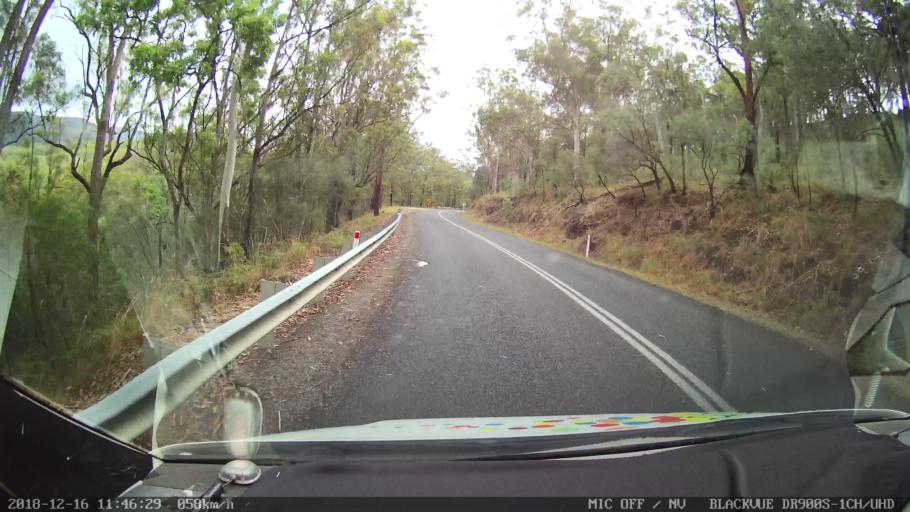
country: AU
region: New South Wales
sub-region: Tenterfield Municipality
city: Carrolls Creek
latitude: -28.9279
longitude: 152.2313
